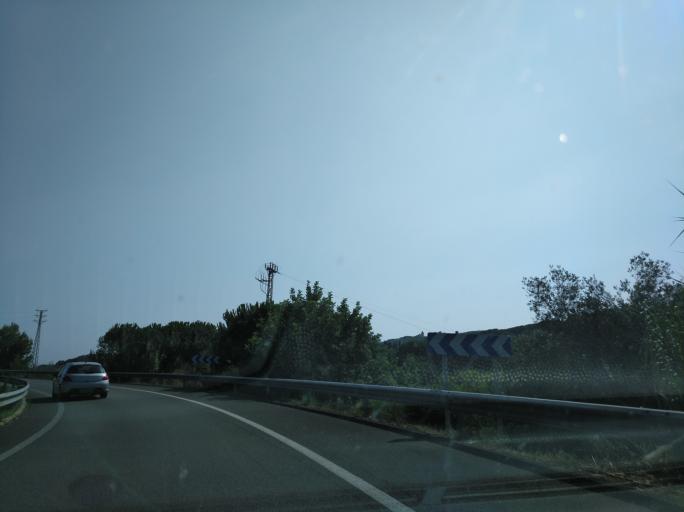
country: ES
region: Catalonia
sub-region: Provincia de Barcelona
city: Argentona
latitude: 41.5458
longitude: 2.4133
